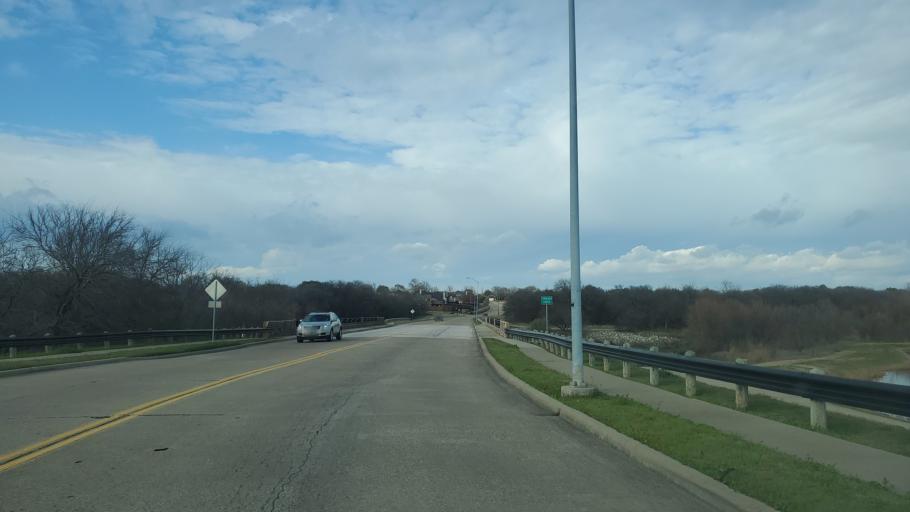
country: US
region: Texas
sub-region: Dallas County
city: Carrollton
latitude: 32.9894
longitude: -96.9020
